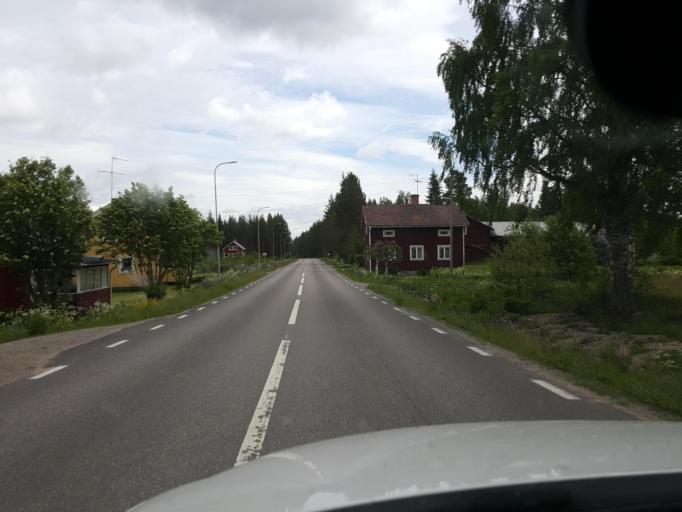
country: SE
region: Gaevleborg
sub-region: Ljusdals Kommun
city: Farila
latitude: 61.7972
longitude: 15.6716
